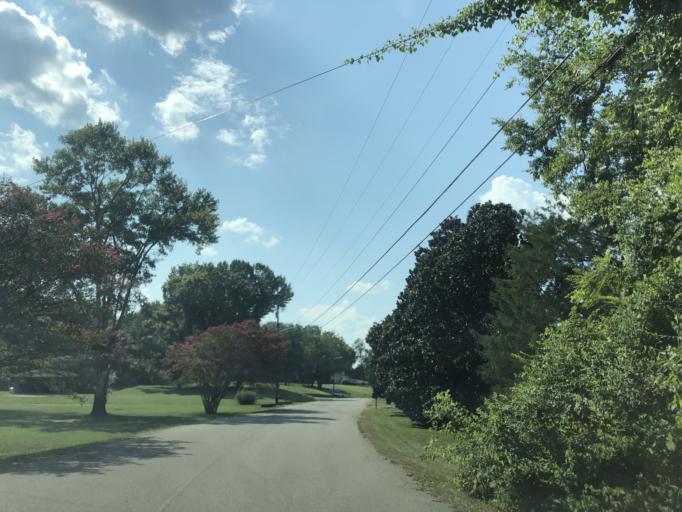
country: US
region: Tennessee
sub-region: Davidson County
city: Oak Hill
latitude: 36.0957
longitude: -86.7667
